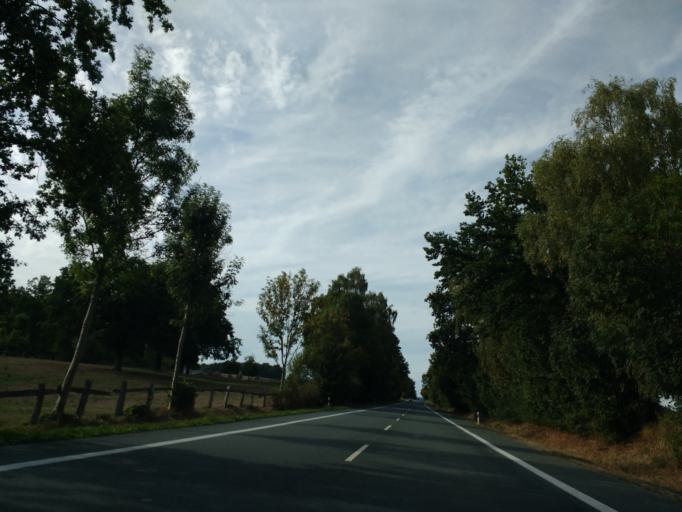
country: DE
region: North Rhine-Westphalia
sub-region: Regierungsbezirk Detmold
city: Nieheim
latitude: 51.8234
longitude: 9.0880
